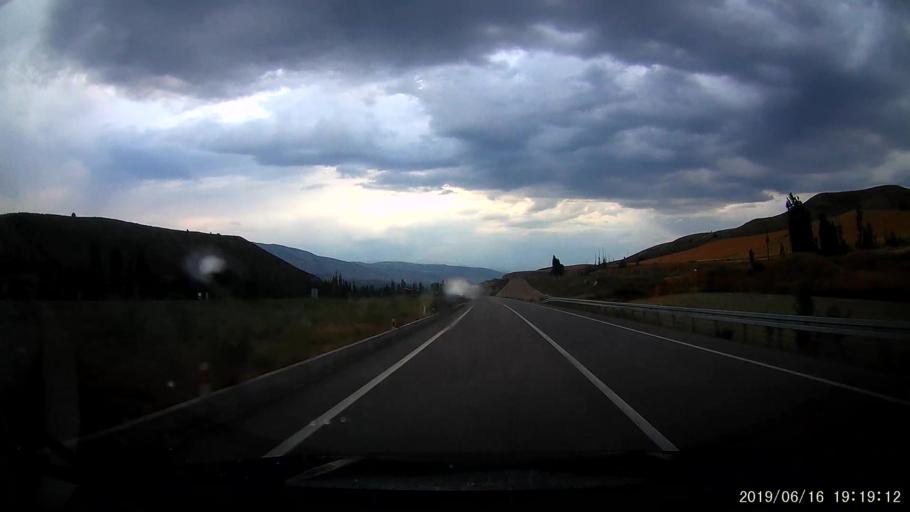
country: TR
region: Sivas
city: Akincilar
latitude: 40.0941
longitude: 38.4376
